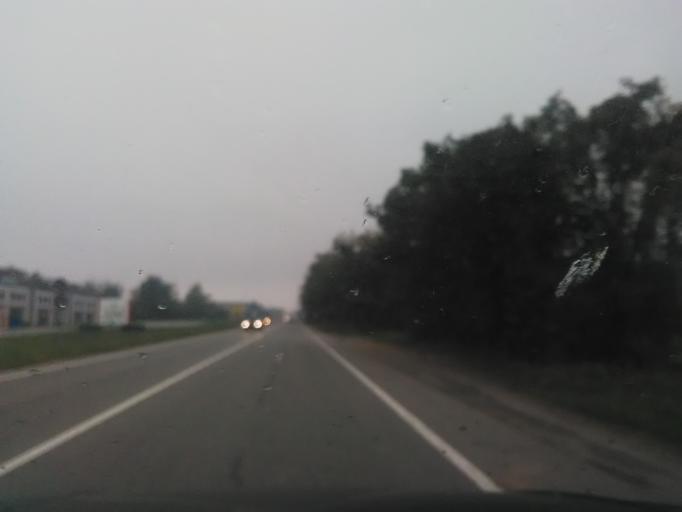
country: IT
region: Piedmont
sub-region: Provincia di Vercelli
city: Santhia
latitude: 45.3874
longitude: 8.1326
